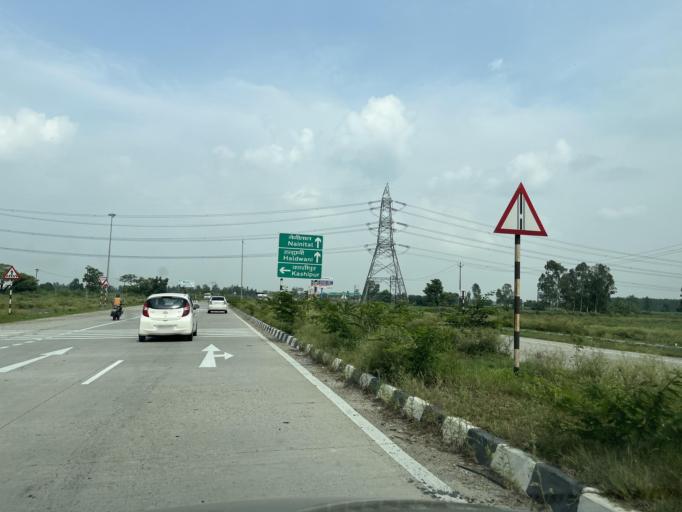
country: IN
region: Uttarakhand
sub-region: Udham Singh Nagar
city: Bazpur
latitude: 29.1497
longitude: 79.0815
